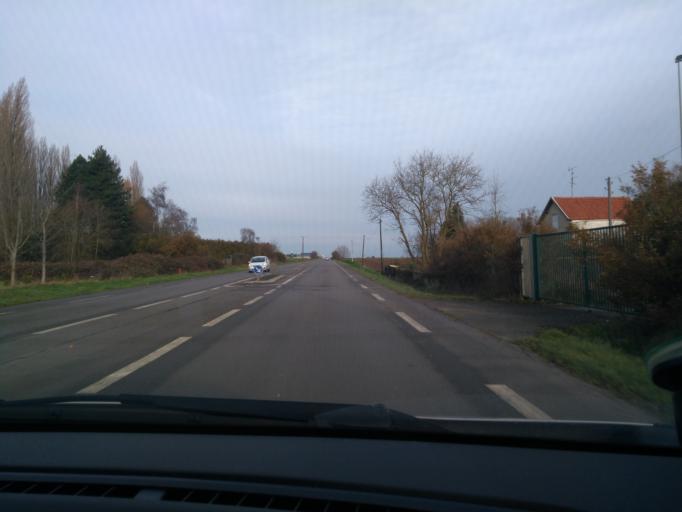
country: FR
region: Nord-Pas-de-Calais
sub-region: Departement du Nord
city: Maubeuge
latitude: 50.3182
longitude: 3.9767
